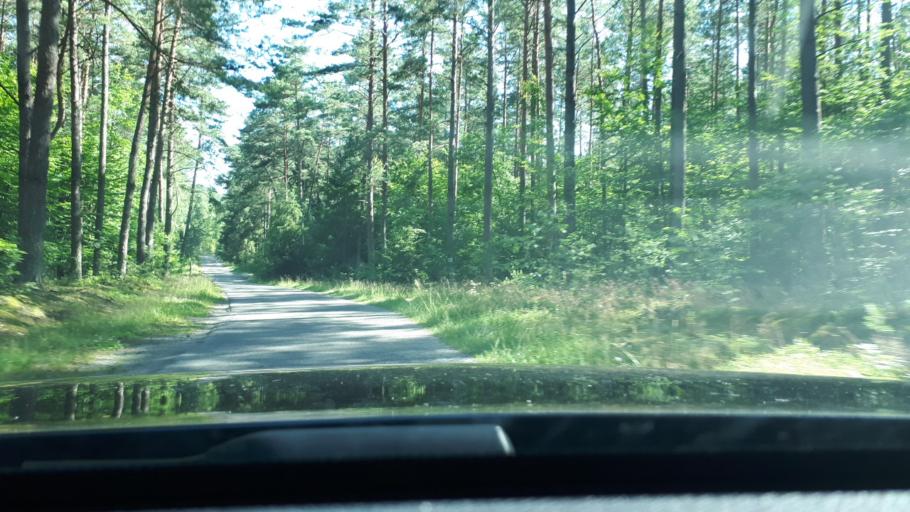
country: PL
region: Warmian-Masurian Voivodeship
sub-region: Powiat olsztynski
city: Stawiguda
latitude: 53.5811
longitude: 20.4519
